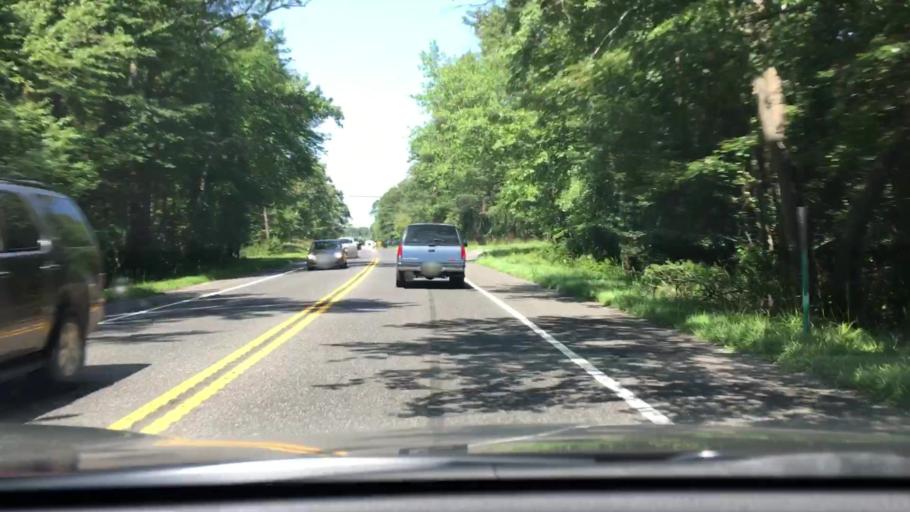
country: US
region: New Jersey
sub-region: Cumberland County
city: Port Norris
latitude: 39.2884
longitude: -74.9611
